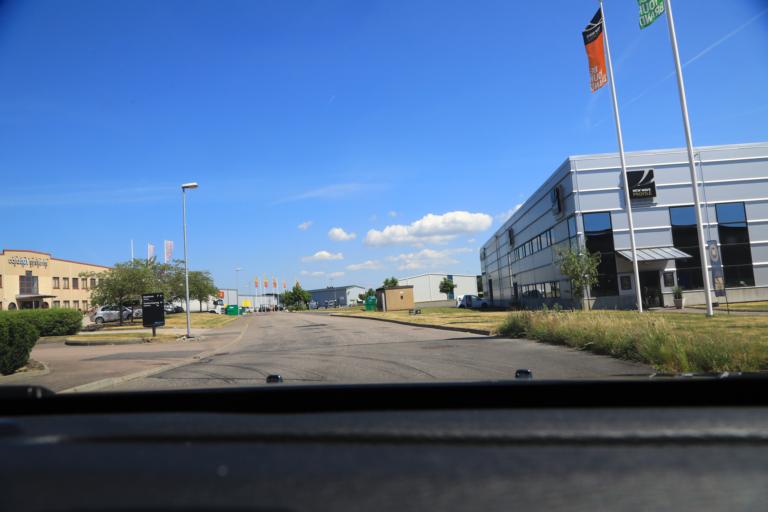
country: SE
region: Halland
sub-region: Kungsbacka Kommun
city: Kungsbacka
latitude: 57.5118
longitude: 12.0667
